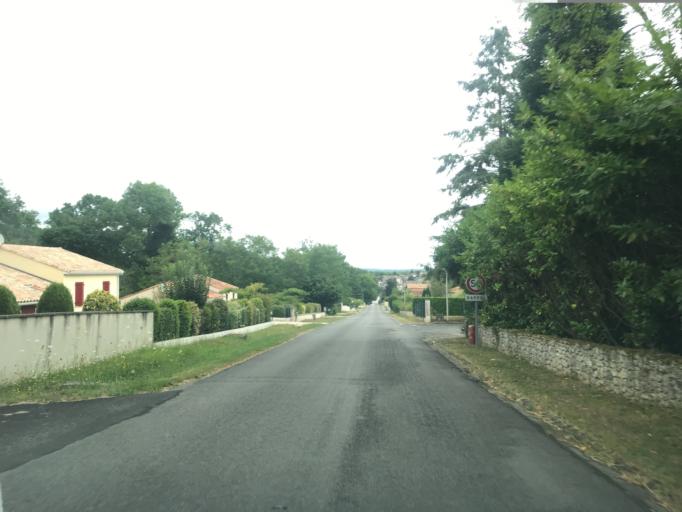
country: FR
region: Poitou-Charentes
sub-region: Departement de la Charente
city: Dignac
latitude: 45.5520
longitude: 0.2721
